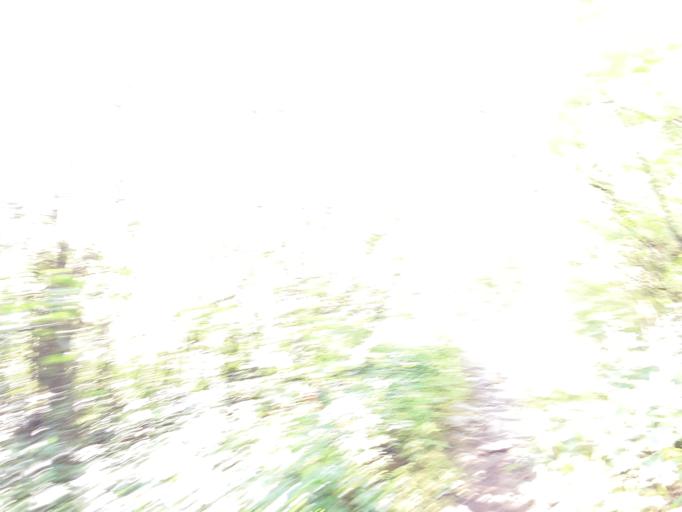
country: CA
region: Ontario
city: Ottawa
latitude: 45.4287
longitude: -75.7431
